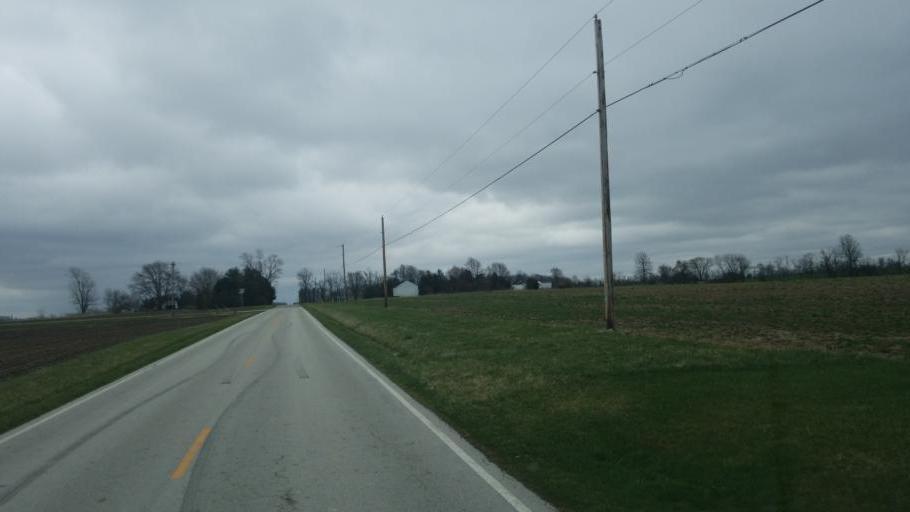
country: US
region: Ohio
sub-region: Wyandot County
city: Upper Sandusky
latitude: 40.8261
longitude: -83.1716
